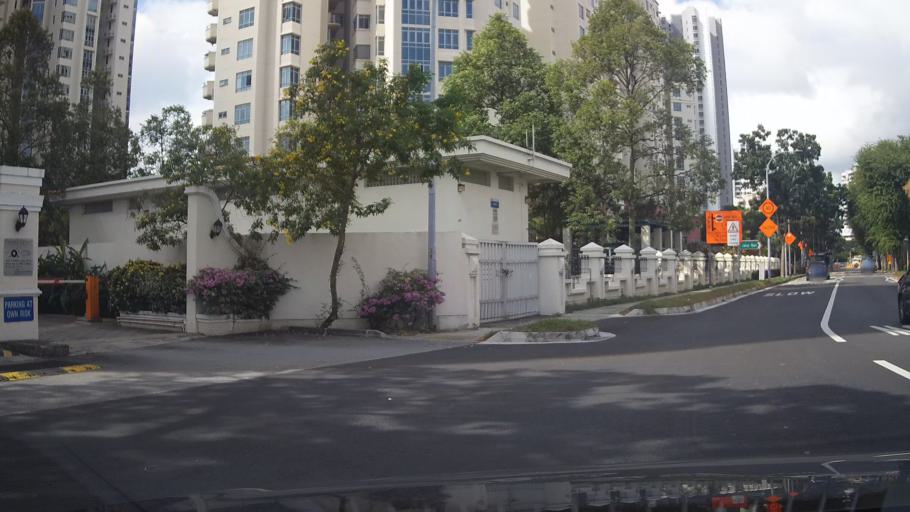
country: SG
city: Singapore
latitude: 1.2984
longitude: 103.8954
